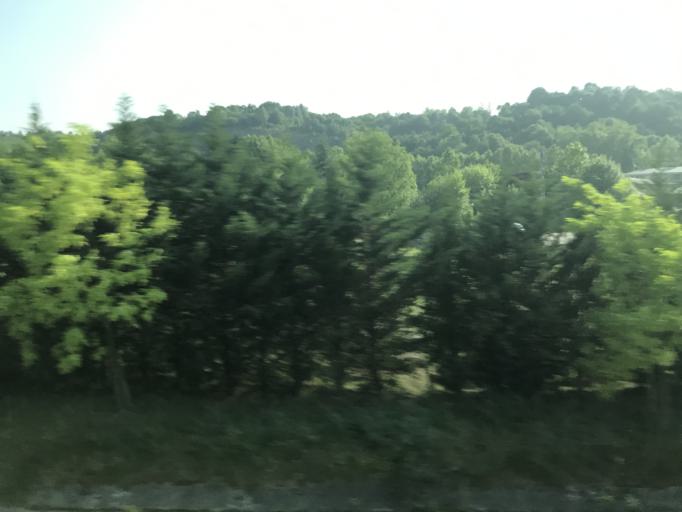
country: ES
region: Basque Country
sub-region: Provincia de Guipuzcoa
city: San Sebastian
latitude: 43.3033
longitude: -1.9614
